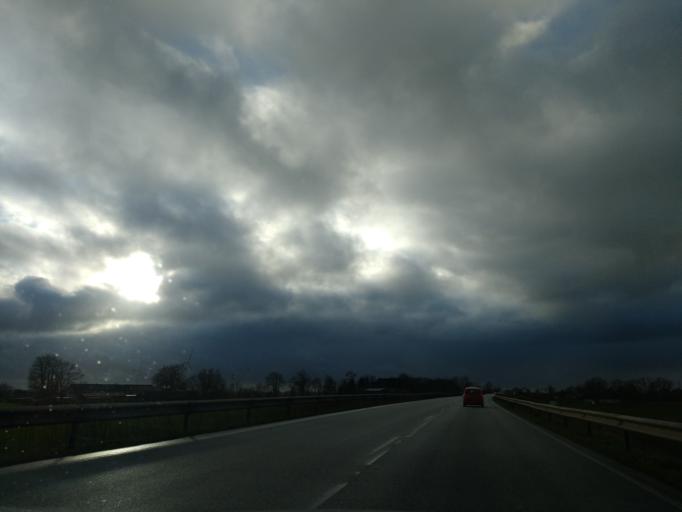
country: DE
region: Schleswig-Holstein
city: Wilster
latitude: 53.9181
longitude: 9.3944
